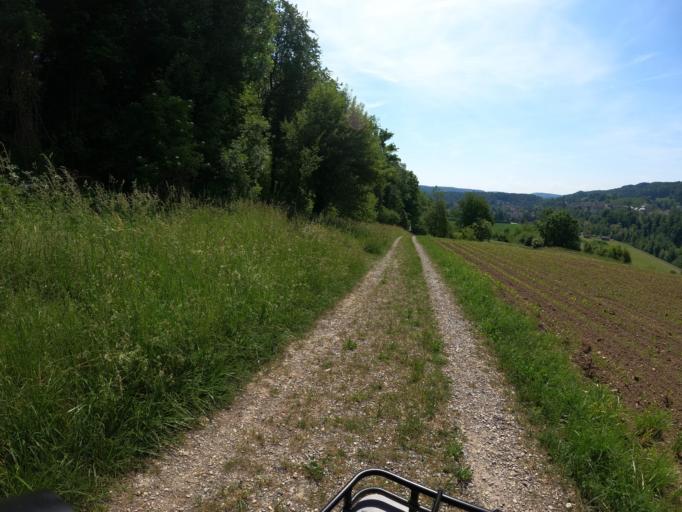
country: CH
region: Zurich
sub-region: Bezirk Buelach
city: Rorbas
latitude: 47.5413
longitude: 8.5709
